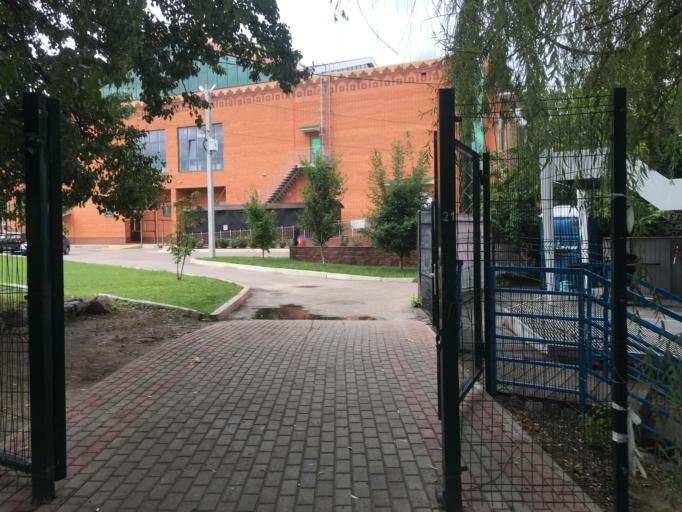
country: RU
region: Voronezj
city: Rossosh'
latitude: 50.1975
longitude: 39.5751
